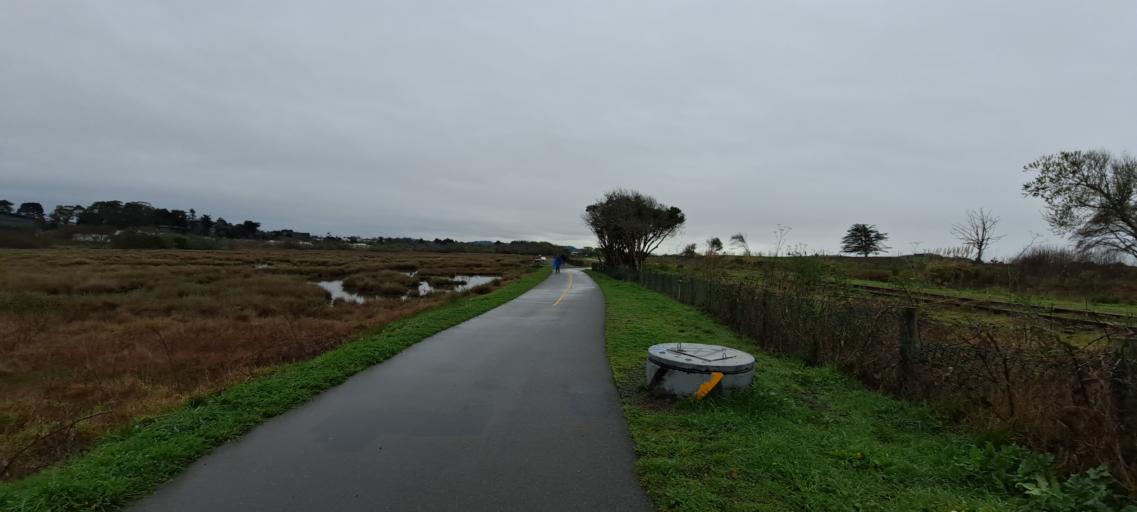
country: US
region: California
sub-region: Humboldt County
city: Bayview
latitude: 40.7899
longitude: -124.1855
